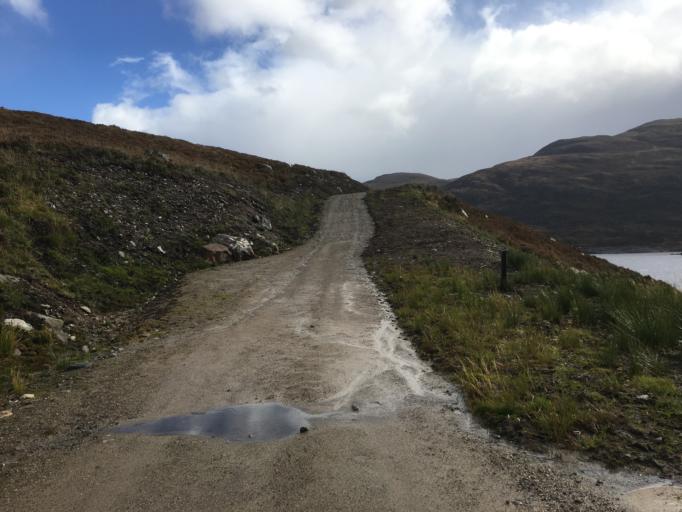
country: GB
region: Scotland
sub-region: Highland
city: Spean Bridge
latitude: 57.3406
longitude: -4.9728
